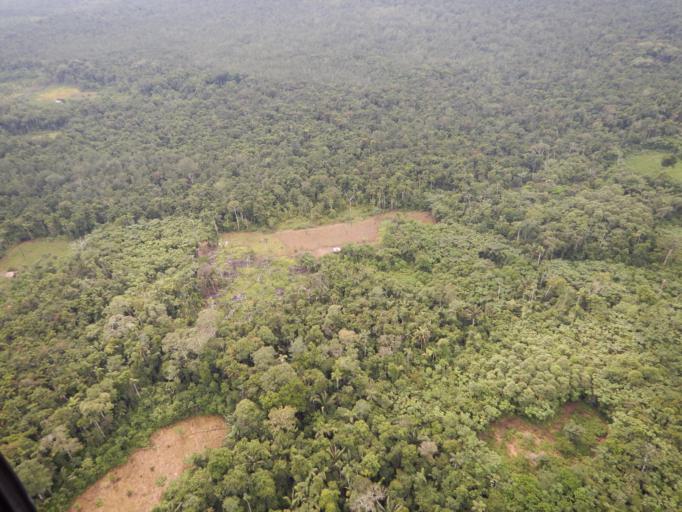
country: BO
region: Cochabamba
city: Chimore
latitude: -16.9199
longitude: -64.9331
